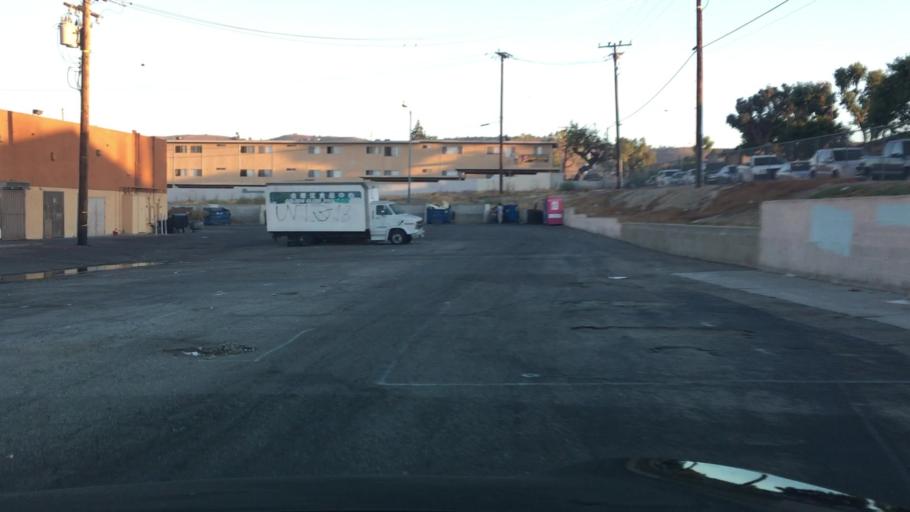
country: US
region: California
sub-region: Los Angeles County
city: Rowland Heights
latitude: 33.9867
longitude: -117.9038
